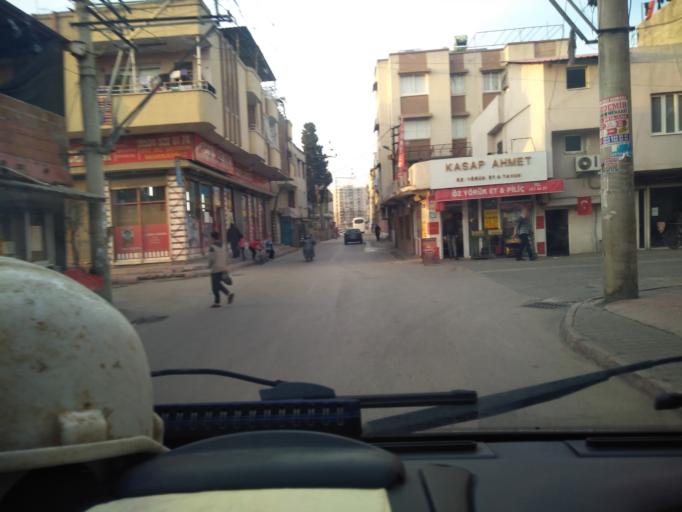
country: TR
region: Adana
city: Seyhan
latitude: 37.0030
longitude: 35.2799
